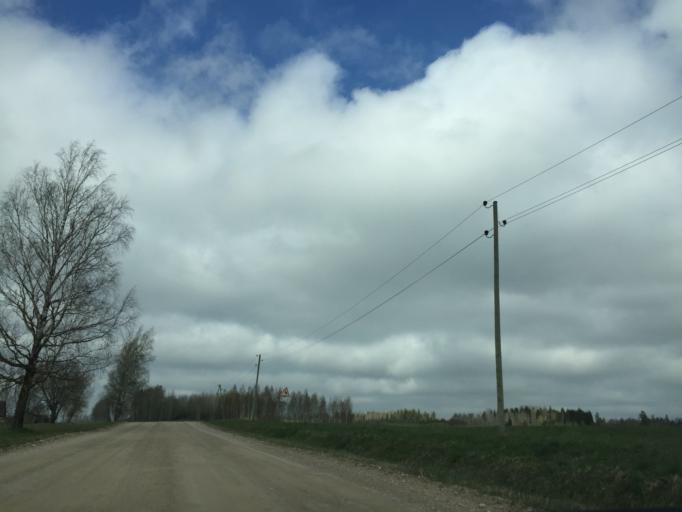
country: EE
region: Valgamaa
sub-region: Valga linn
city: Valga
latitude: 57.5598
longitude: 26.2782
